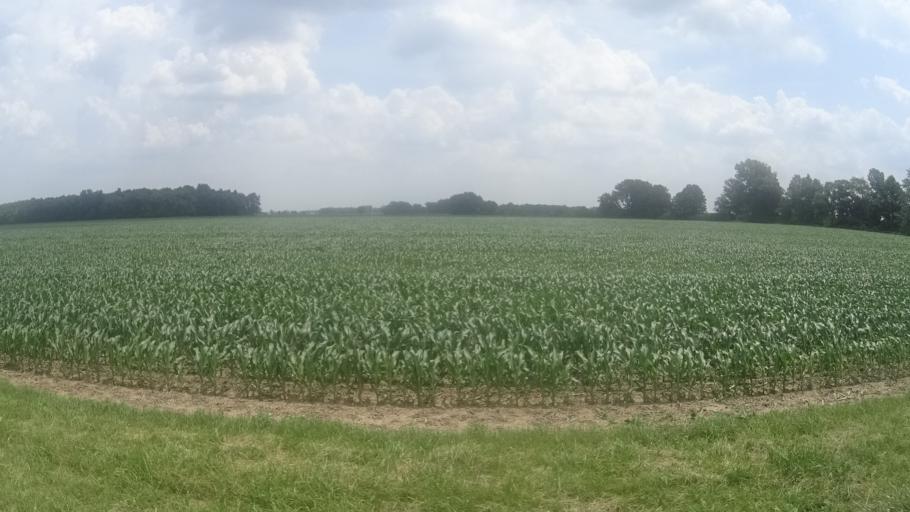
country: US
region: Ohio
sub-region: Huron County
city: Monroeville
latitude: 41.3145
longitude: -82.6928
